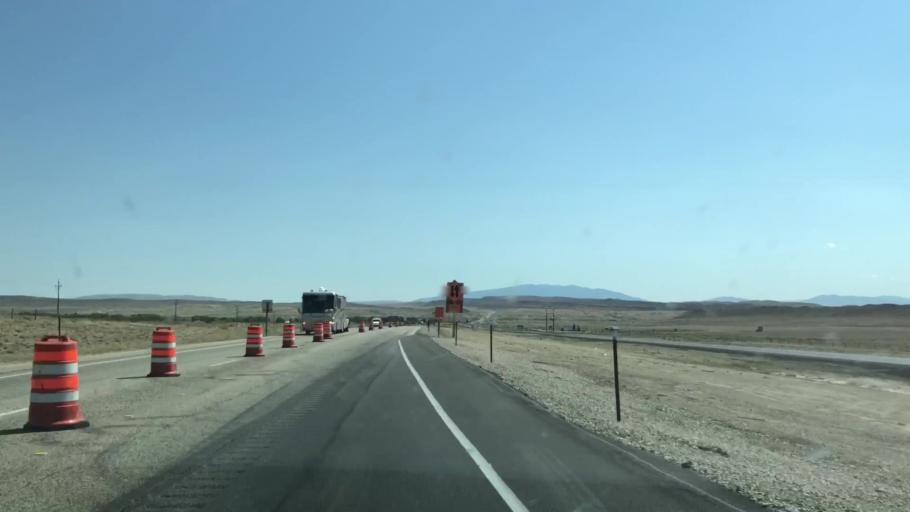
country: US
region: Wyoming
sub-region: Carbon County
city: Rawlins
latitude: 41.7563
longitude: -106.9734
